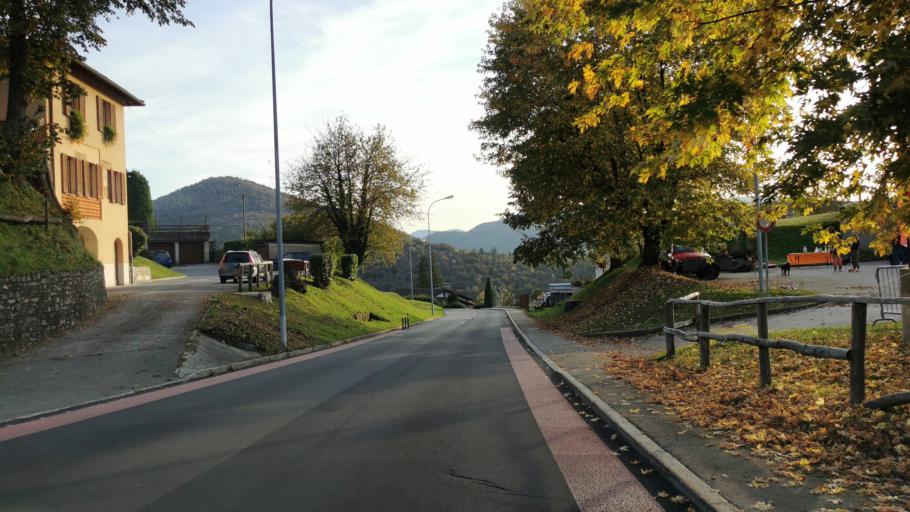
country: CH
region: Ticino
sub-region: Lugano District
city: Pura
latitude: 46.0083
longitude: 8.8590
